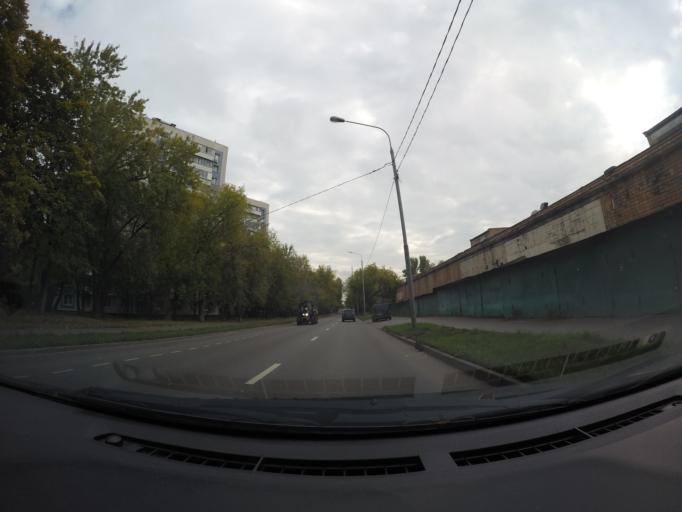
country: RU
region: Moscow
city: Lefortovo
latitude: 55.7640
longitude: 37.7284
